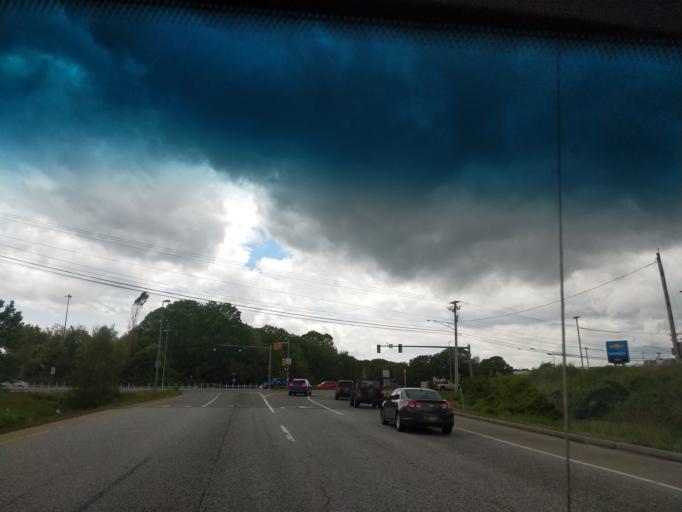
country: US
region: Maine
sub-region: Cumberland County
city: South Portland Gardens
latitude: 43.6321
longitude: -70.3113
